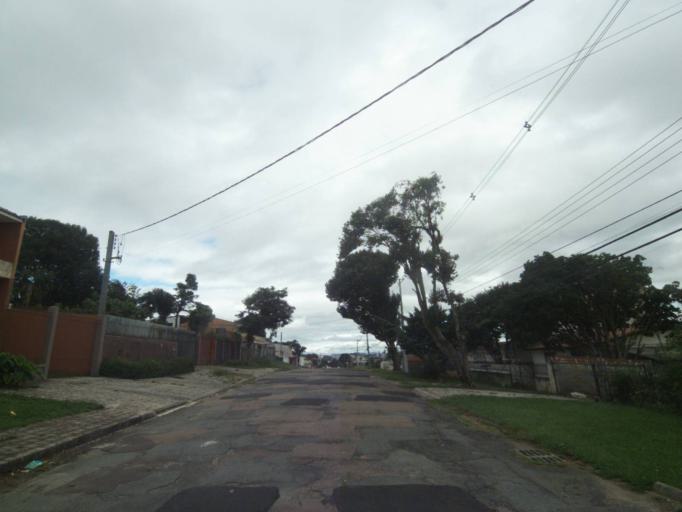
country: BR
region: Parana
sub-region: Curitiba
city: Curitiba
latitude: -25.4775
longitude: -49.2740
